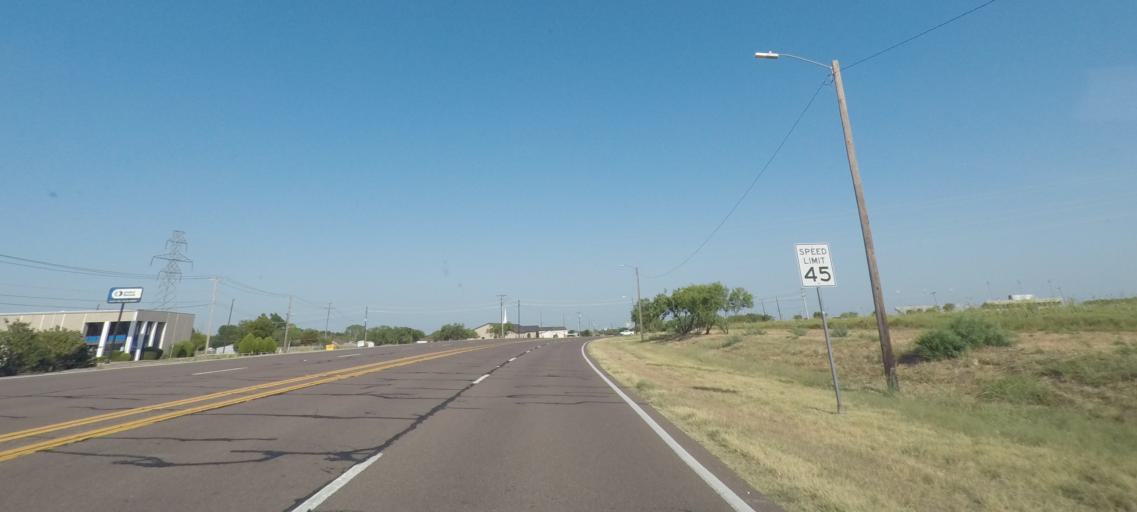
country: US
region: Texas
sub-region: Wichita County
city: Wichita Falls
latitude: 33.8592
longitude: -98.5889
